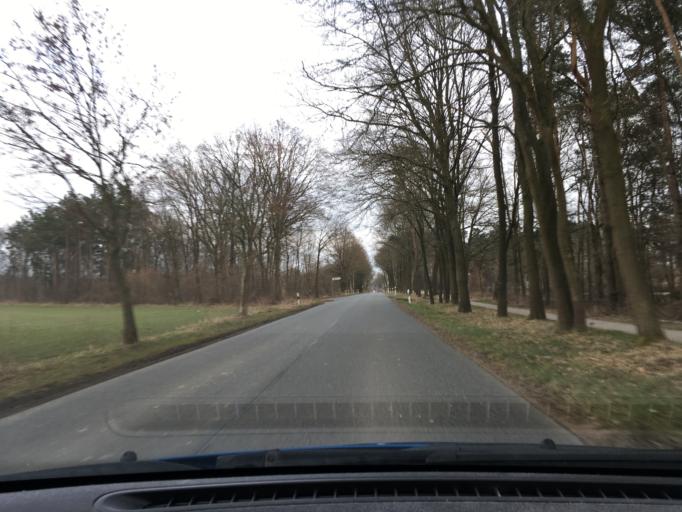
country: DE
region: Lower Saxony
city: Reppenstedt
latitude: 53.2518
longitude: 10.3318
